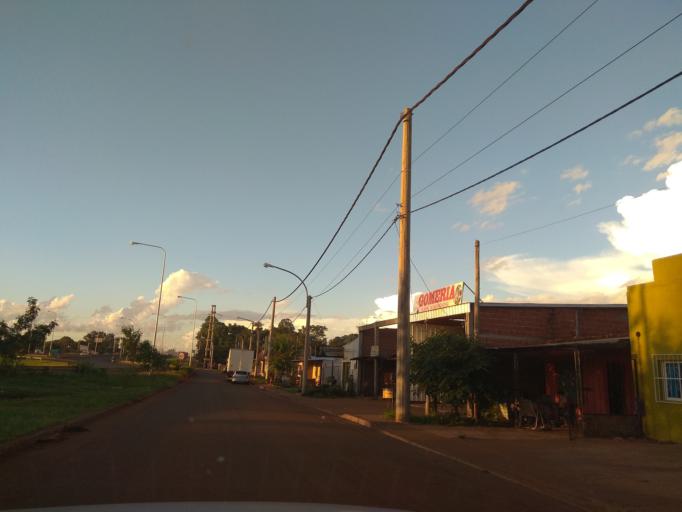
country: AR
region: Misiones
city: Garupa
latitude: -27.4646
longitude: -55.8627
